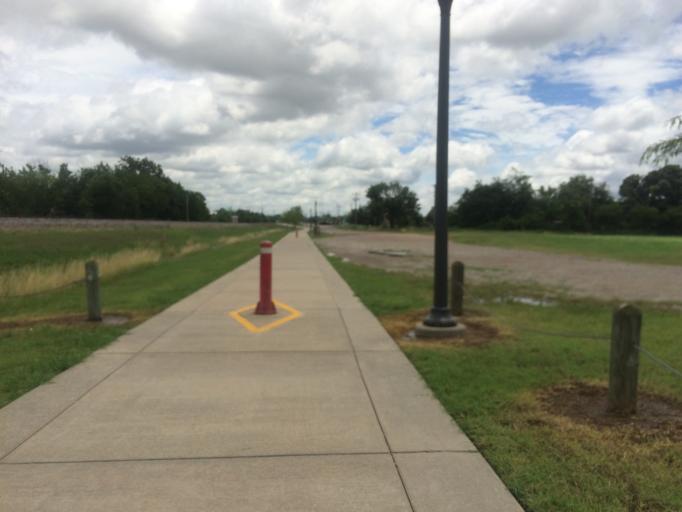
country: US
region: Oklahoma
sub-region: Cleveland County
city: Norman
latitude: 35.2272
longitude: -97.4479
